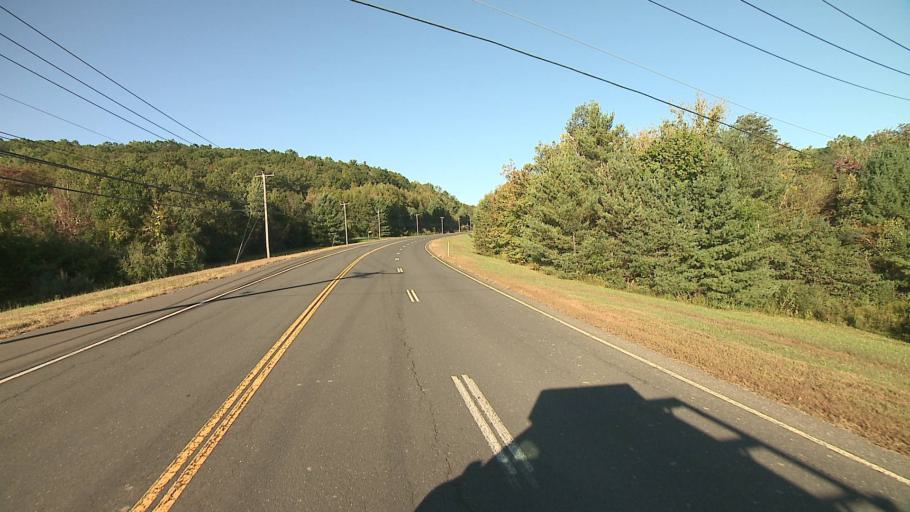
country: US
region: Connecticut
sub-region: Litchfield County
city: New Hartford Center
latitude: 41.8285
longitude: -73.0083
